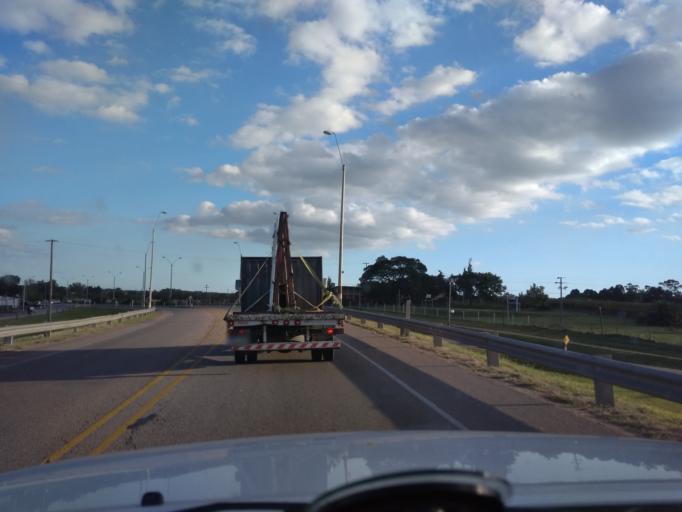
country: UY
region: Canelones
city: Canelones
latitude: -34.5439
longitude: -56.2746
